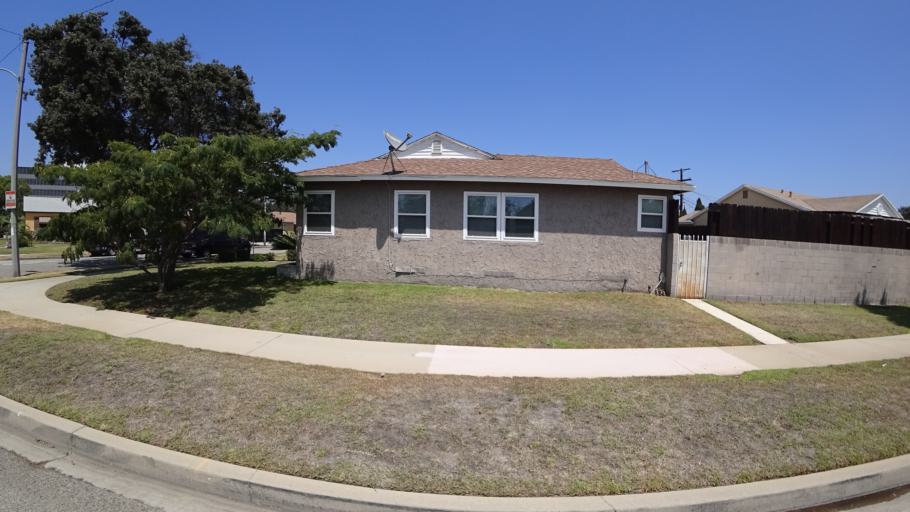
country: US
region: California
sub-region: Los Angeles County
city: Lennox
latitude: 33.9295
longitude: -118.3316
